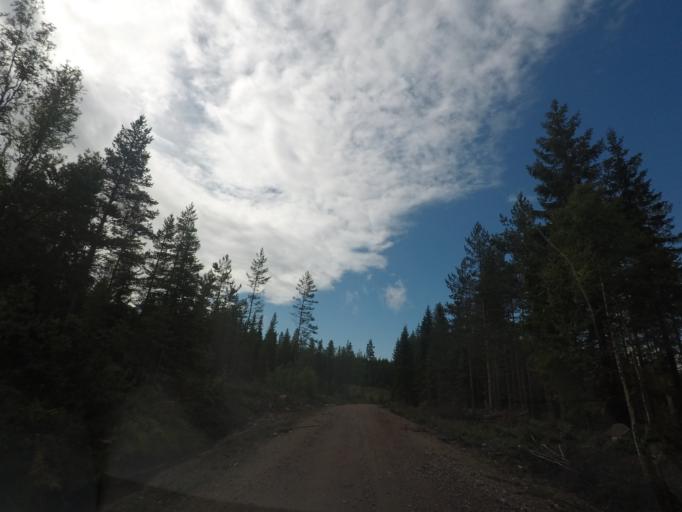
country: SE
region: Vaermland
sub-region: Filipstads Kommun
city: Lesjofors
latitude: 60.0955
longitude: 14.3841
